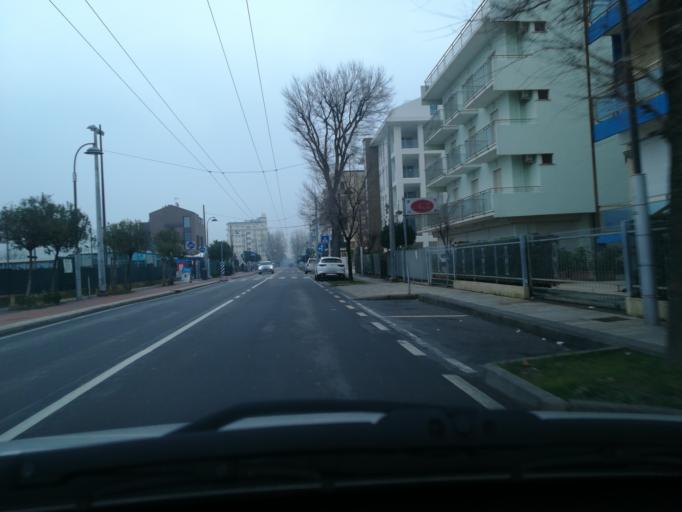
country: IT
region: Emilia-Romagna
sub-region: Provincia di Rimini
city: Riccione
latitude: 44.0175
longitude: 12.6399
